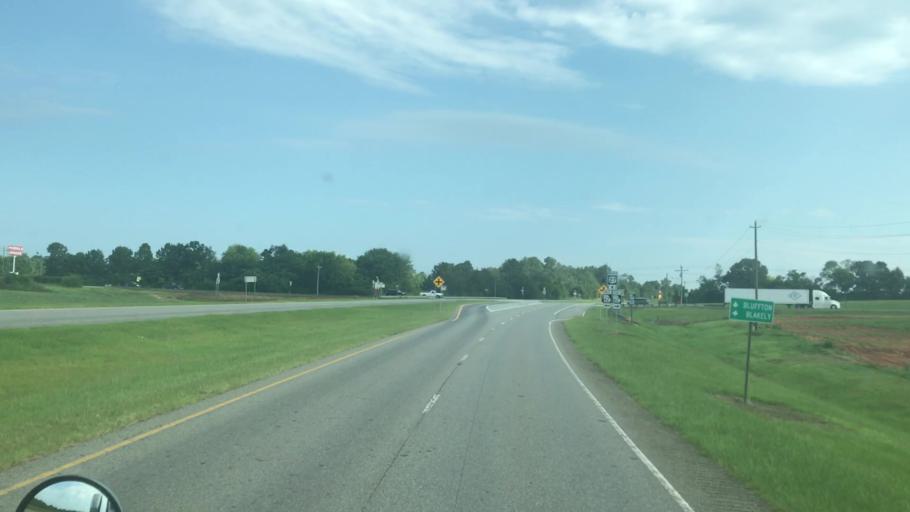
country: US
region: Georgia
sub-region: Early County
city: Blakely
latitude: 31.3898
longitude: -84.9240
